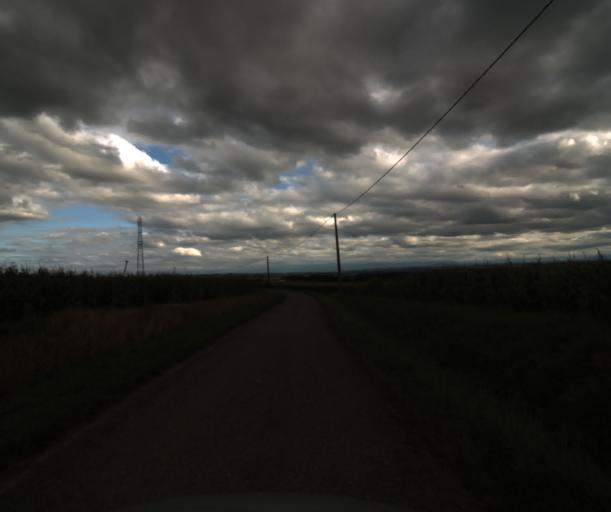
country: FR
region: Midi-Pyrenees
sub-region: Departement de la Haute-Garonne
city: Le Fauga
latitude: 43.3988
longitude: 1.3194
